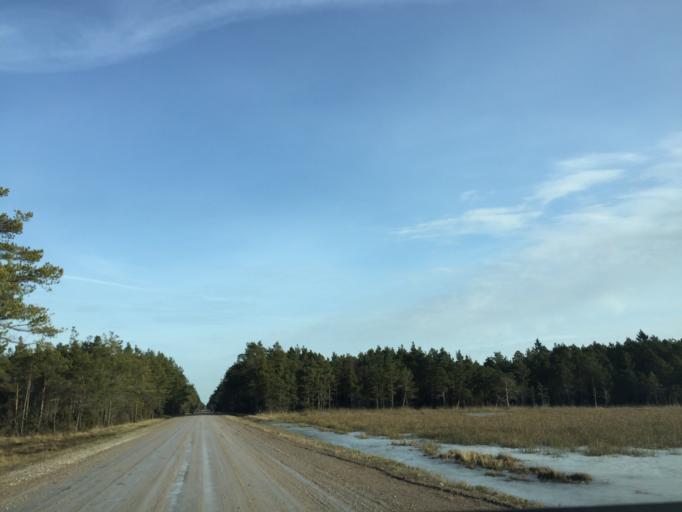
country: EE
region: Saare
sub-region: Kuressaare linn
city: Kuressaare
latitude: 58.3005
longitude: 21.9573
